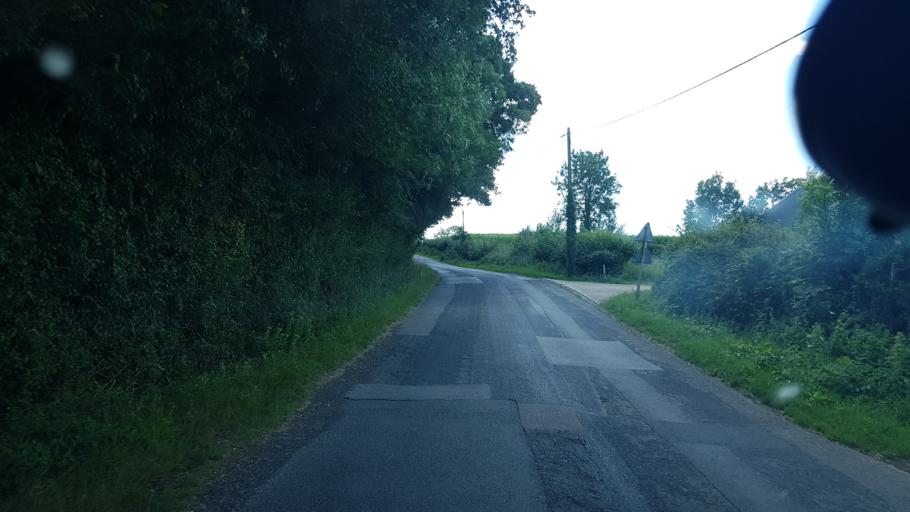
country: GB
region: England
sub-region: Kent
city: Edenbridge
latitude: 51.1937
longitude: 0.1402
